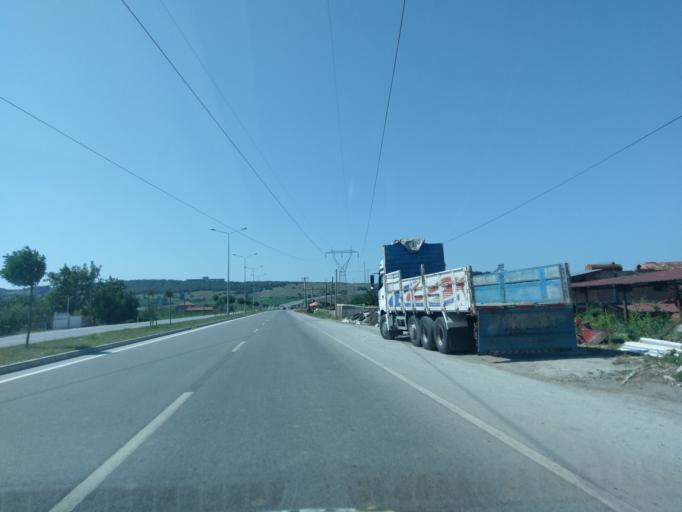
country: TR
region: Samsun
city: Bafra
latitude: 41.5766
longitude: 35.8564
